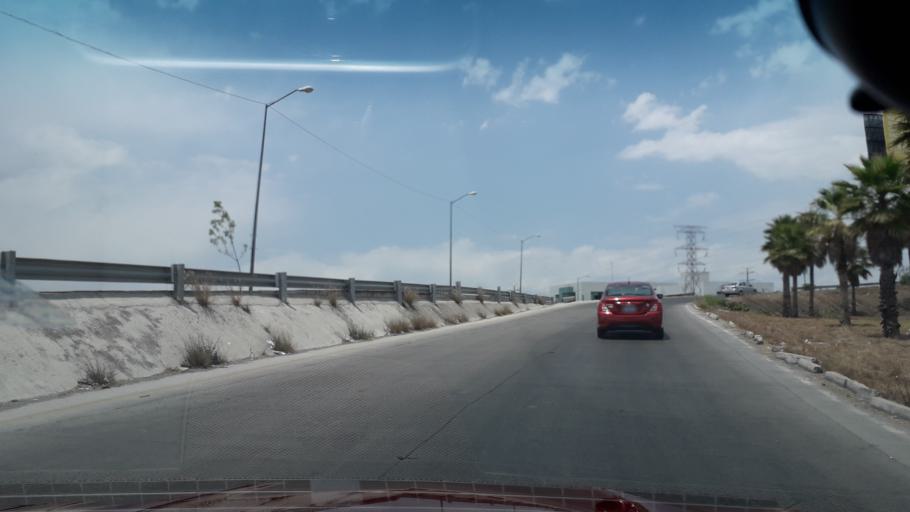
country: MX
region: Puebla
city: Tlazcalancingo
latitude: 19.0189
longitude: -98.2503
